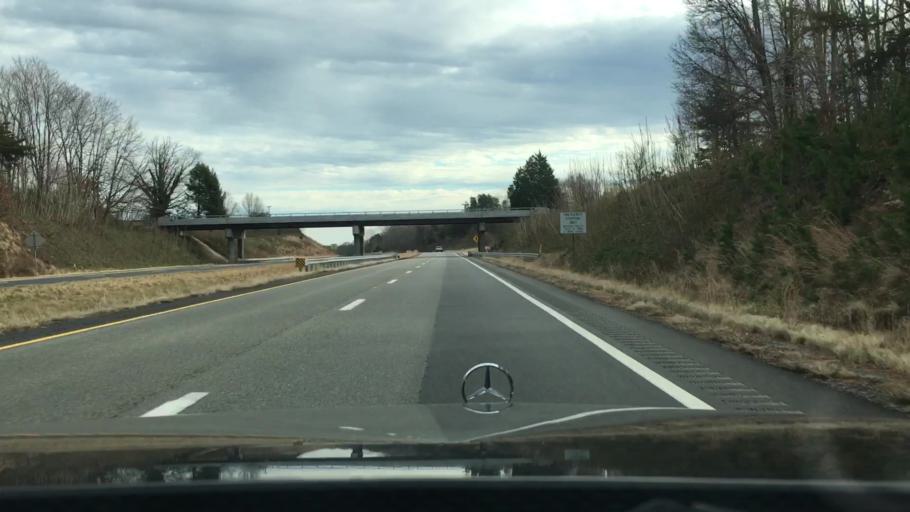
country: US
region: Virginia
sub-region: Pittsylvania County
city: Chatham
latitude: 36.8500
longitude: -79.3944
